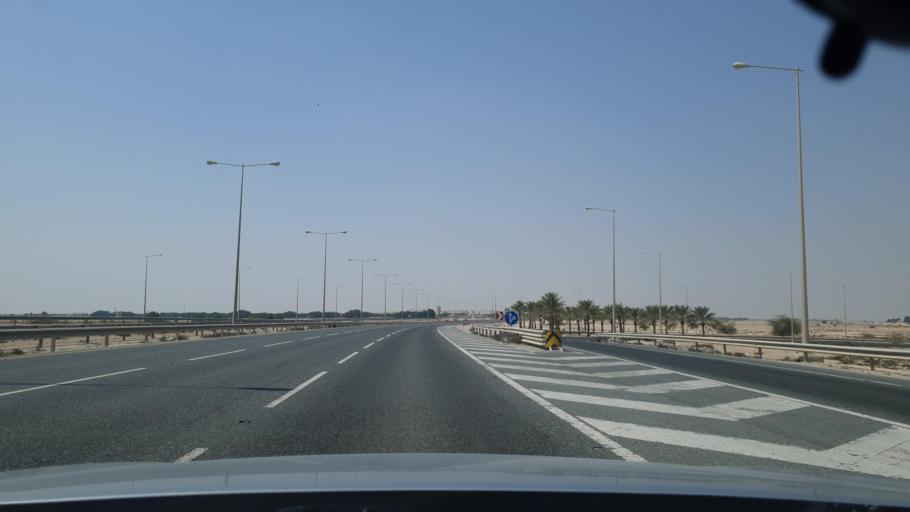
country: QA
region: Al Khawr
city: Al Khawr
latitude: 25.7540
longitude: 51.4381
